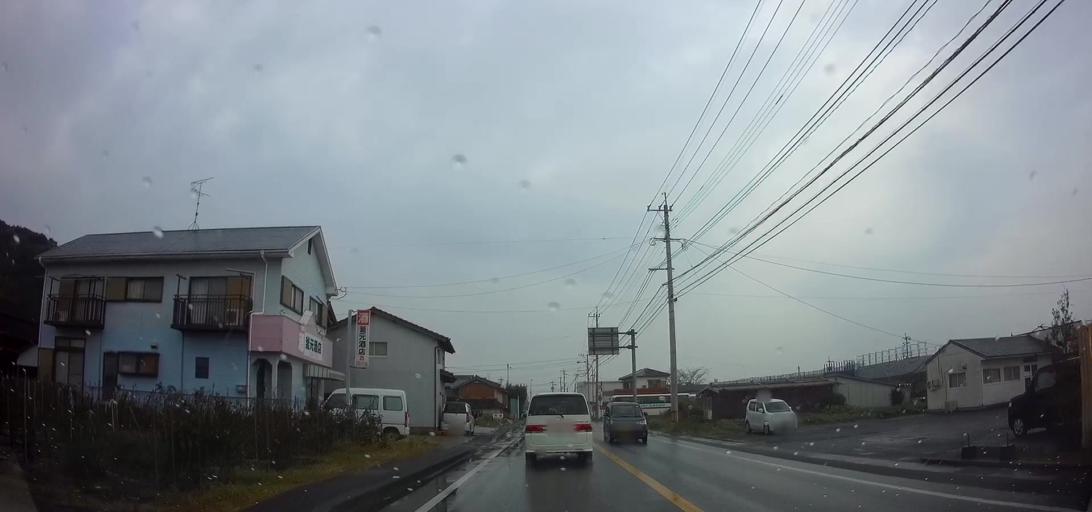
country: JP
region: Nagasaki
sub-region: Isahaya-shi
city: Isahaya
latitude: 32.8325
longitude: 130.1367
